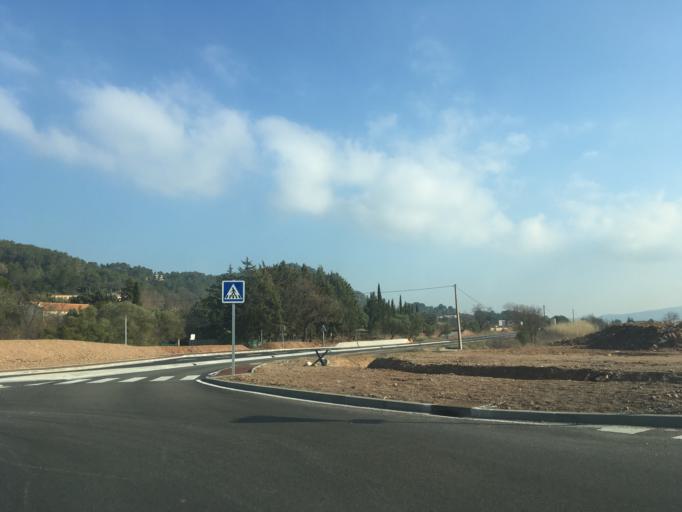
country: FR
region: Provence-Alpes-Cote d'Azur
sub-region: Departement du Var
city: Vidauban
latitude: 43.4033
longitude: 6.3933
